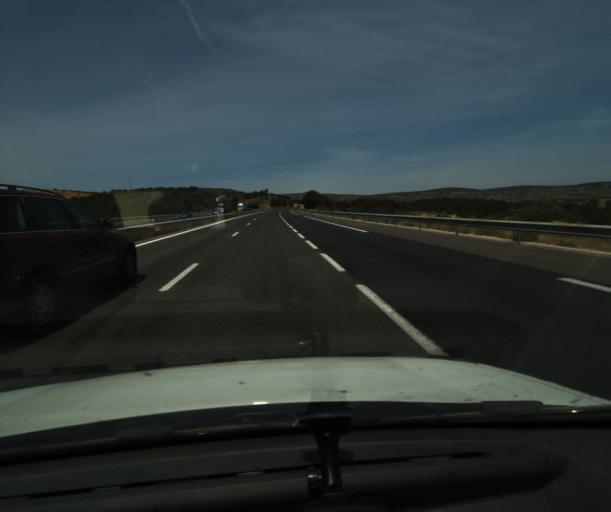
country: FR
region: Languedoc-Roussillon
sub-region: Departement des Pyrenees-Orientales
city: Salses-le-Chateau
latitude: 42.8344
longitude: 2.9103
